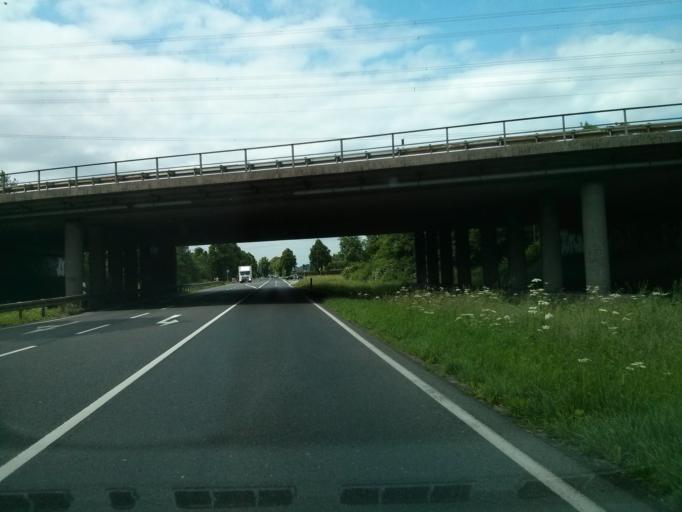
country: DE
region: North Rhine-Westphalia
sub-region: Regierungsbezirk Dusseldorf
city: Krefeld
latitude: 51.2864
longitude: 6.6070
